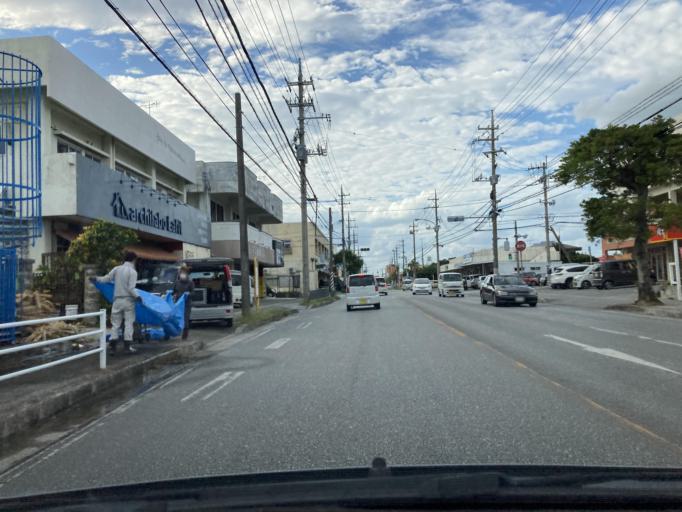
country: JP
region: Okinawa
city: Okinawa
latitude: 26.3581
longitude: 127.8256
